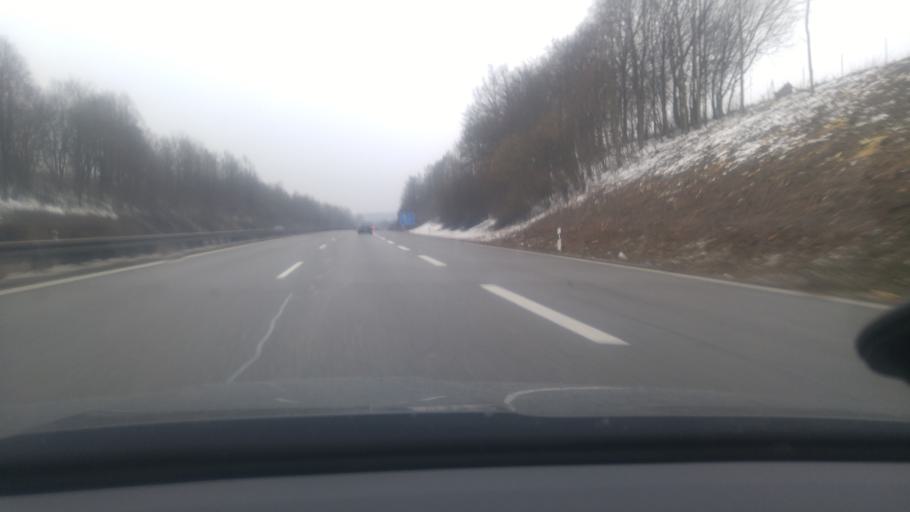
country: DE
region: Baden-Wuerttemberg
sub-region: Karlsruhe Region
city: Empfingen
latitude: 48.4002
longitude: 8.7282
